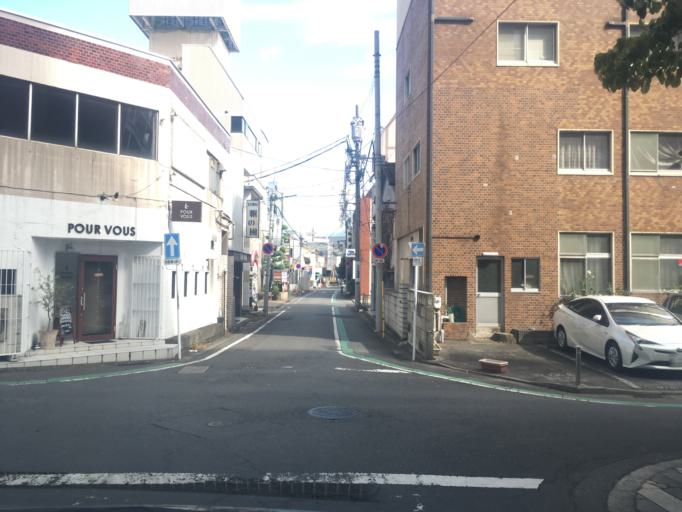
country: JP
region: Gunma
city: Maebashi-shi
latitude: 36.3897
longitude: 139.0722
